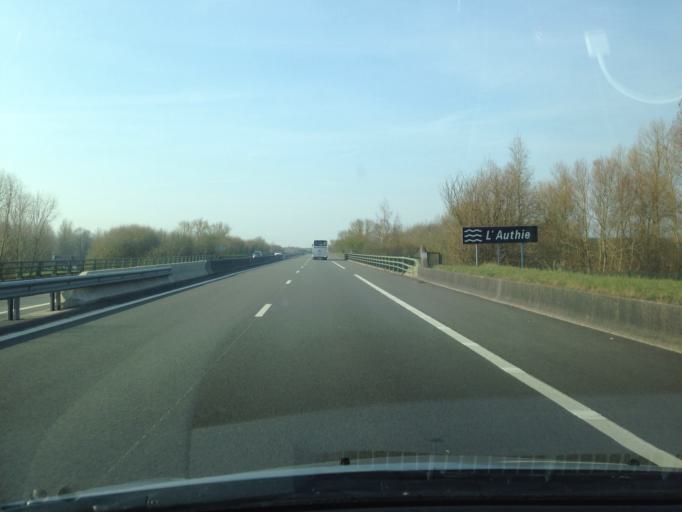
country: FR
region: Picardie
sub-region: Departement de la Somme
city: Quend
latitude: 50.3424
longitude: 1.6940
